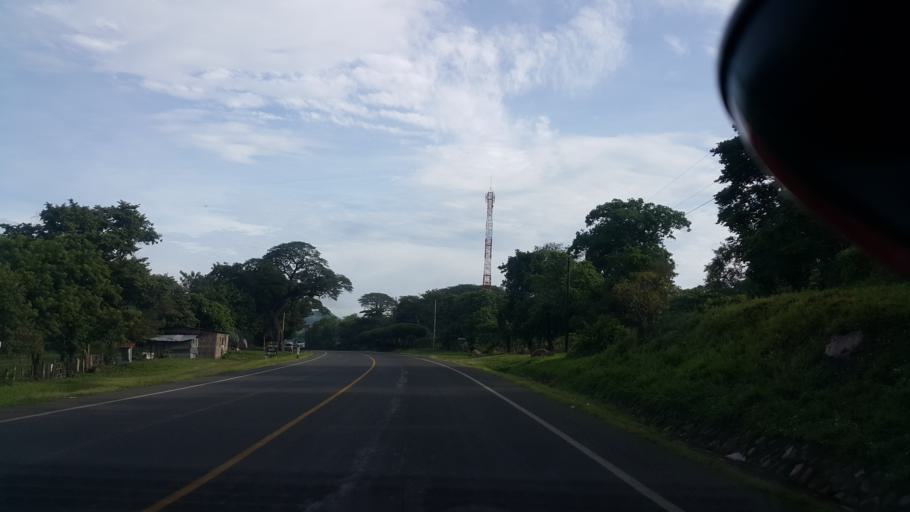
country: NI
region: Matagalpa
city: Terrabona
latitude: 12.5812
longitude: -86.0420
